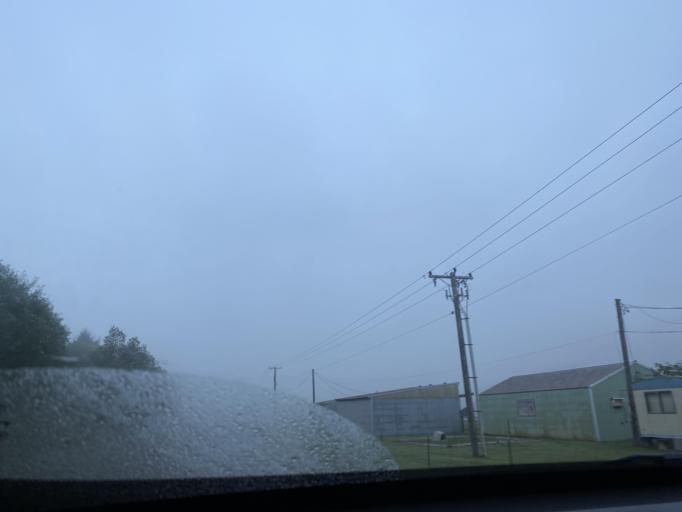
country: US
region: Washington
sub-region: Clallam County
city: Forks
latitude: 47.9365
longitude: -124.3959
